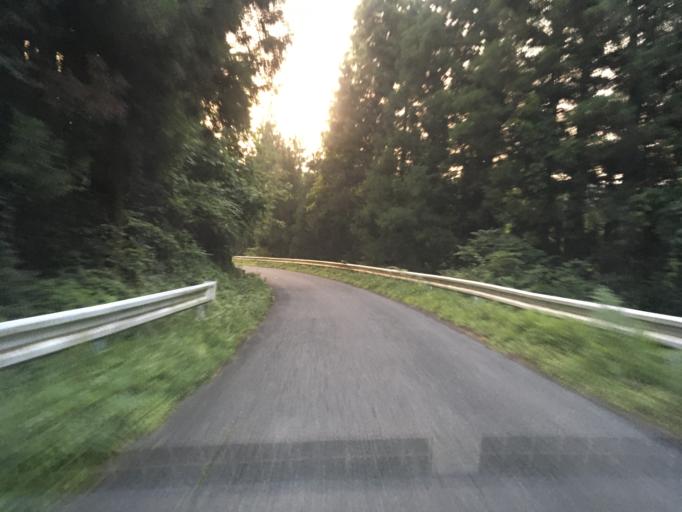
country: JP
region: Iwate
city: Ichinoseki
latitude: 38.8470
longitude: 141.2831
